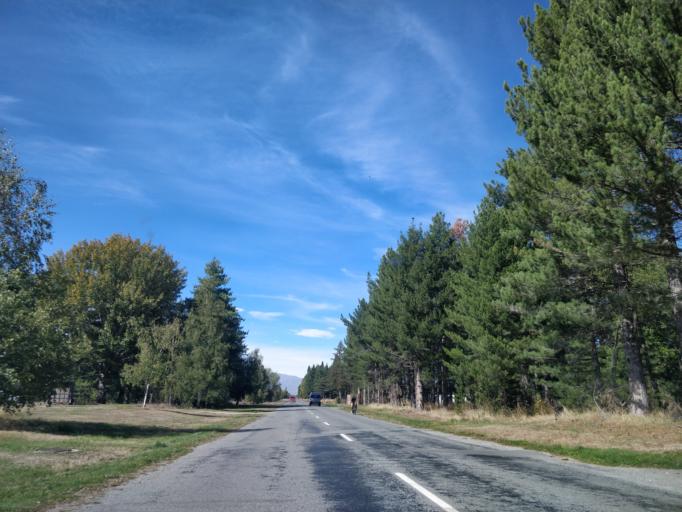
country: NZ
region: Canterbury
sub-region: Timaru District
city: Pleasant Point
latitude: -44.2479
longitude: 170.0963
